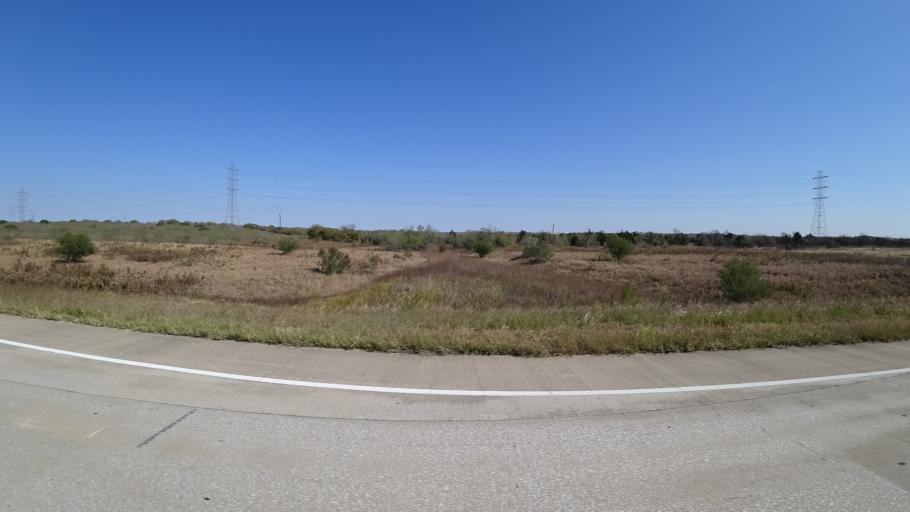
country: US
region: Texas
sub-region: Travis County
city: Onion Creek
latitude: 30.1301
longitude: -97.6645
